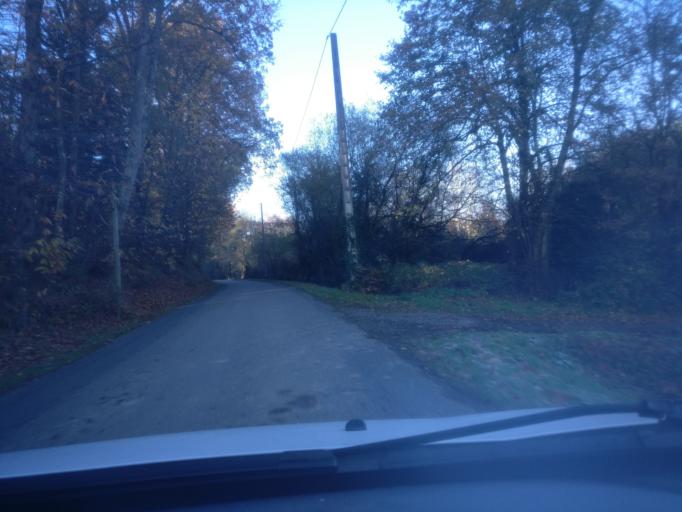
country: FR
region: Brittany
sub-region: Departement d'Ille-et-Vilaine
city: Guichen
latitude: 47.9998
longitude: -1.7832
